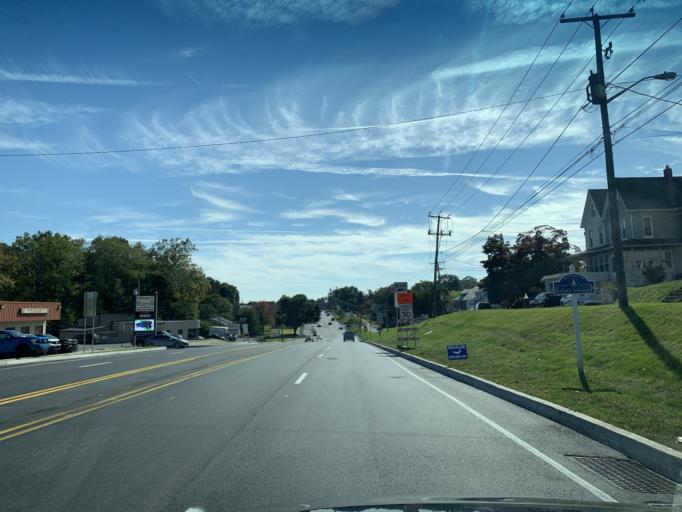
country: US
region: Pennsylvania
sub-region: Berks County
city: Reiffton
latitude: 40.3233
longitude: -75.8764
